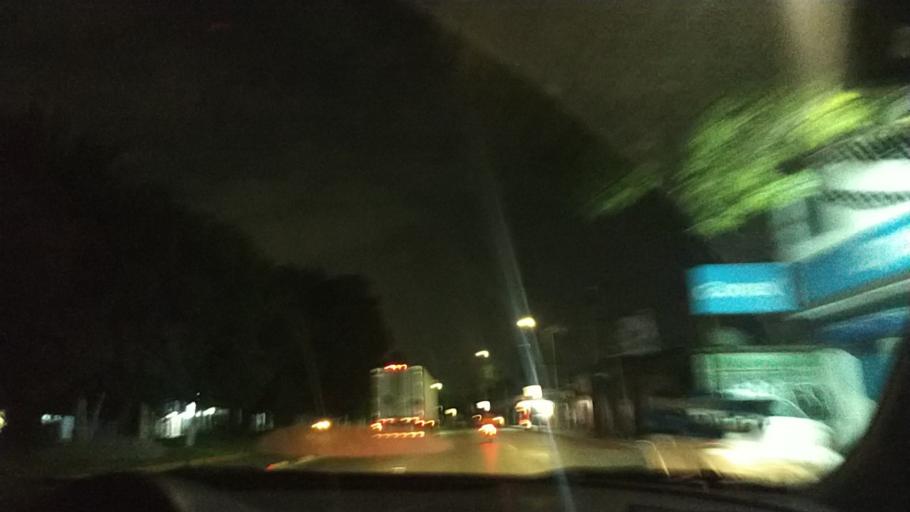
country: MX
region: Mexico
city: Ecatepec
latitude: 19.6144
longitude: -99.0614
